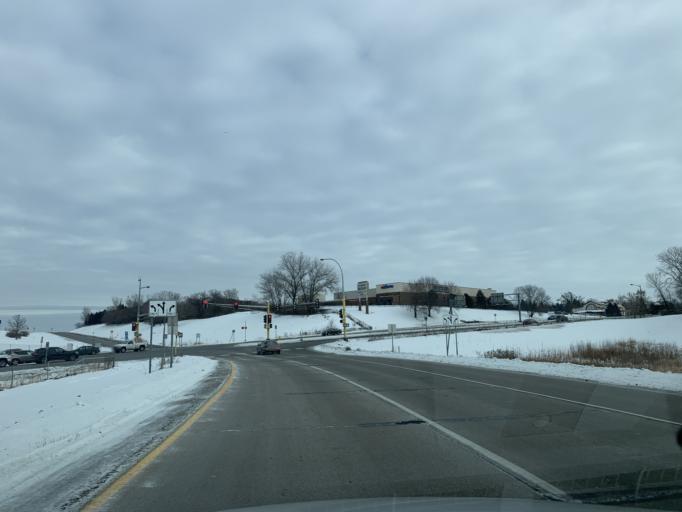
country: US
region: Minnesota
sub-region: Dakota County
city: Burnsville
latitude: 44.7426
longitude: -93.2773
